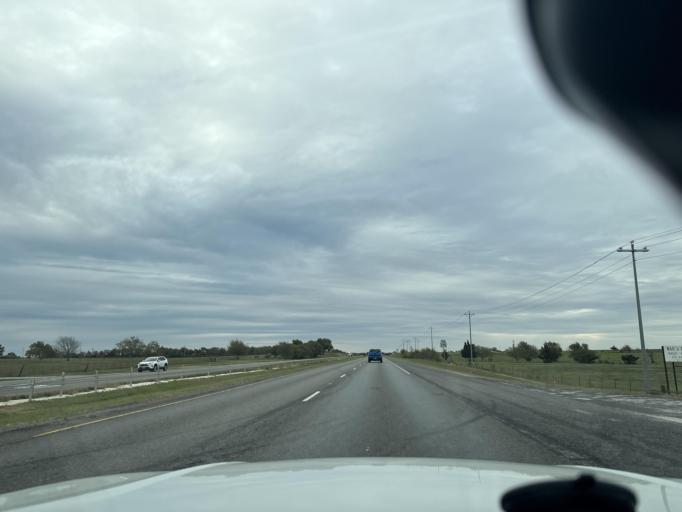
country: US
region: Texas
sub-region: Burleson County
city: Somerville
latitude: 30.1627
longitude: -96.6162
